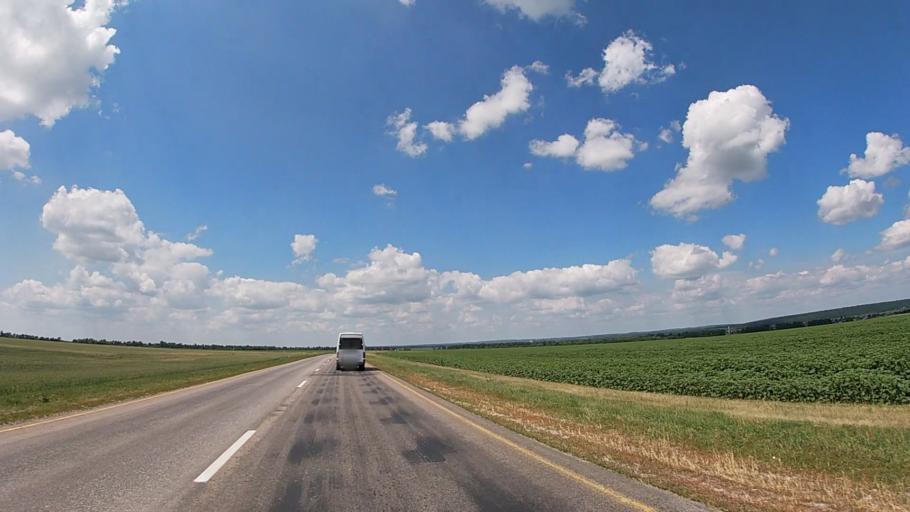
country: RU
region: Belgorod
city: Borisovka
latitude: 50.5760
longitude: 36.0226
